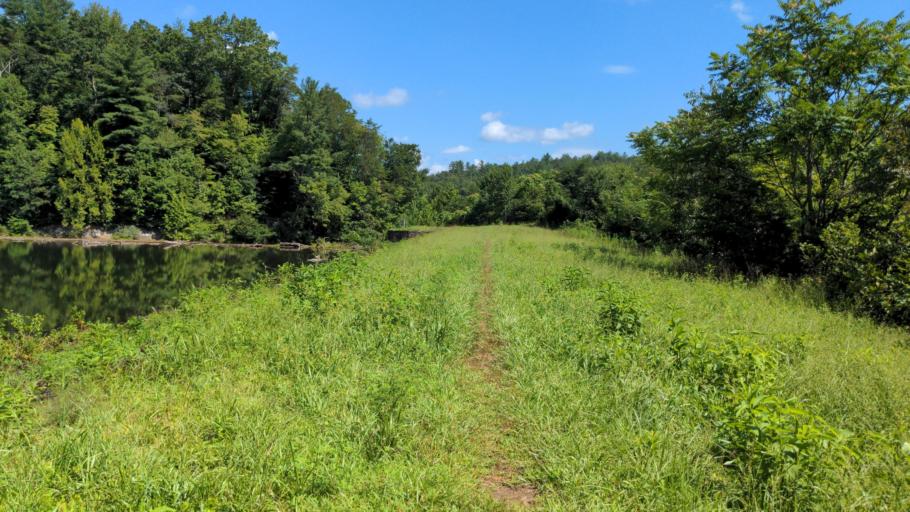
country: US
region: Virginia
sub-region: Henry County
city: Bassett
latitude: 36.7989
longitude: -80.1002
